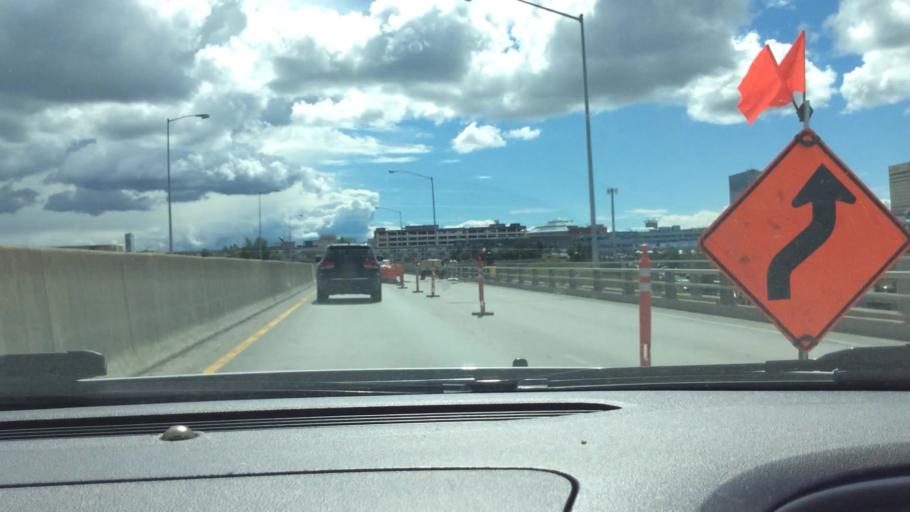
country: US
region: Alaska
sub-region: Anchorage Municipality
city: Anchorage
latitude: 61.2234
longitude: -149.8852
